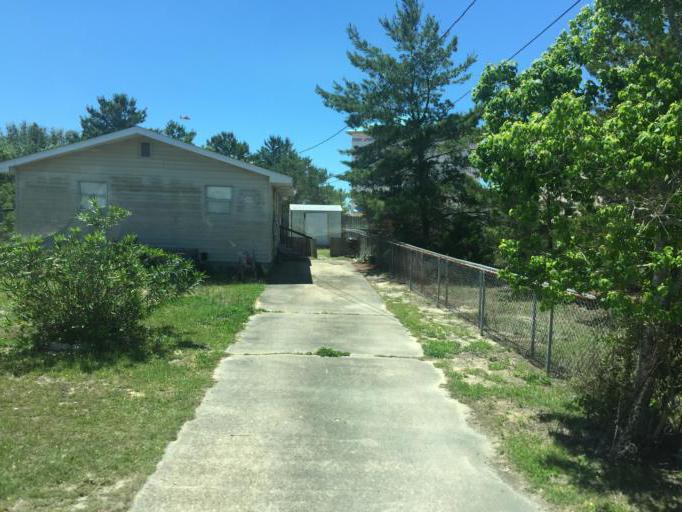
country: US
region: Florida
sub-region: Bay County
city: Laguna Beach
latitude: 30.2560
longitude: -85.9543
